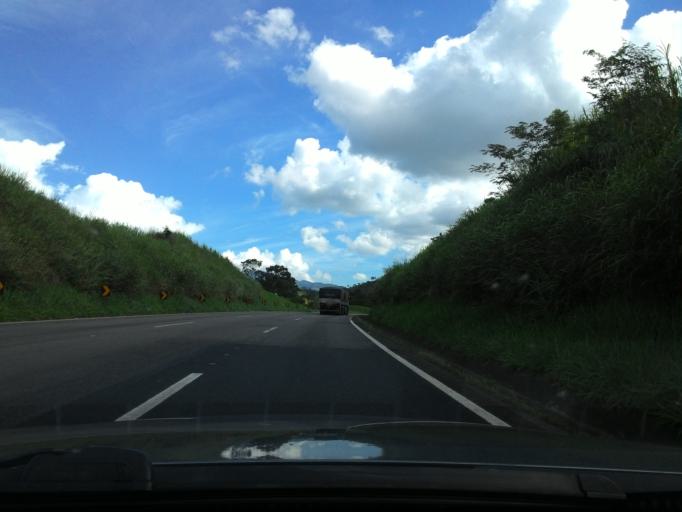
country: BR
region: Sao Paulo
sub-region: Cajati
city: Cajati
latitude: -24.8015
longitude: -48.2132
